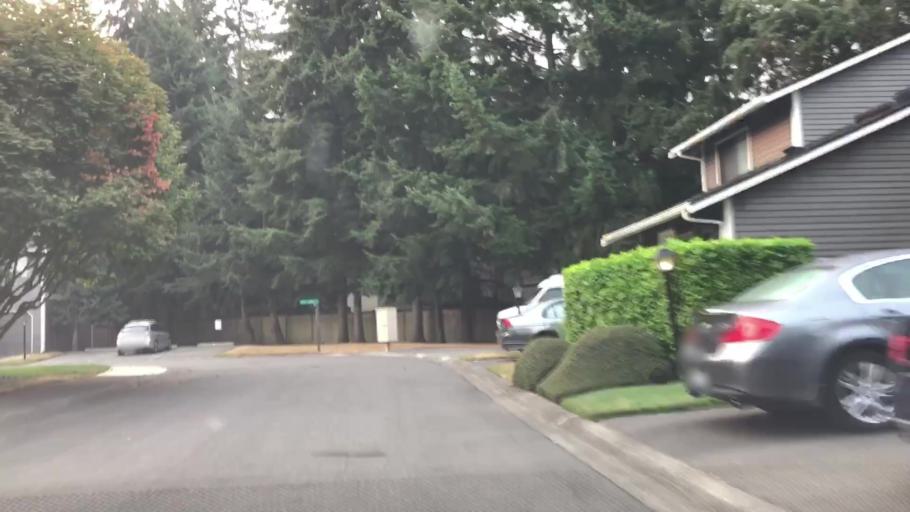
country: US
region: Washington
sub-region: King County
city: Kingsgate
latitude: 47.7176
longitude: -122.1895
